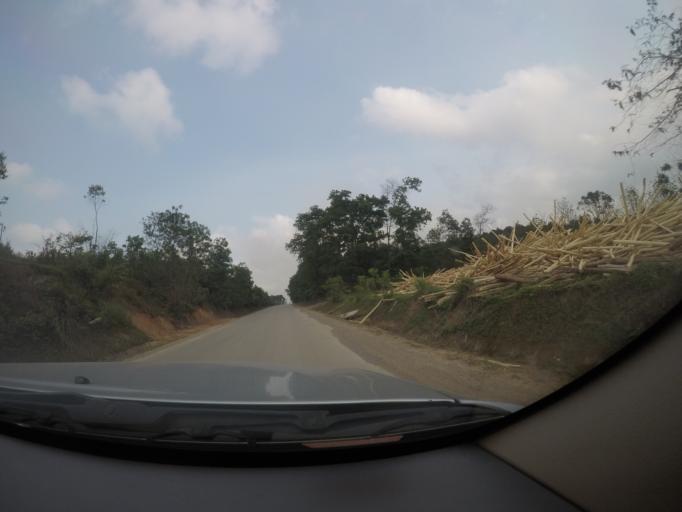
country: VN
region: Quang Binh
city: Kien Giang
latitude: 17.1196
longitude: 106.8236
